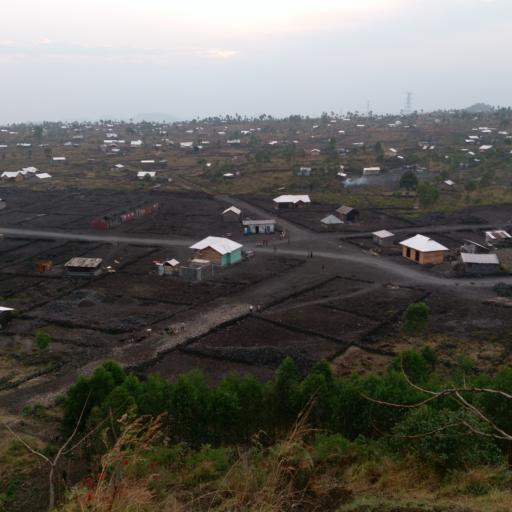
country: CD
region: Nord Kivu
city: Goma
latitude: -1.6303
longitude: 29.2238
